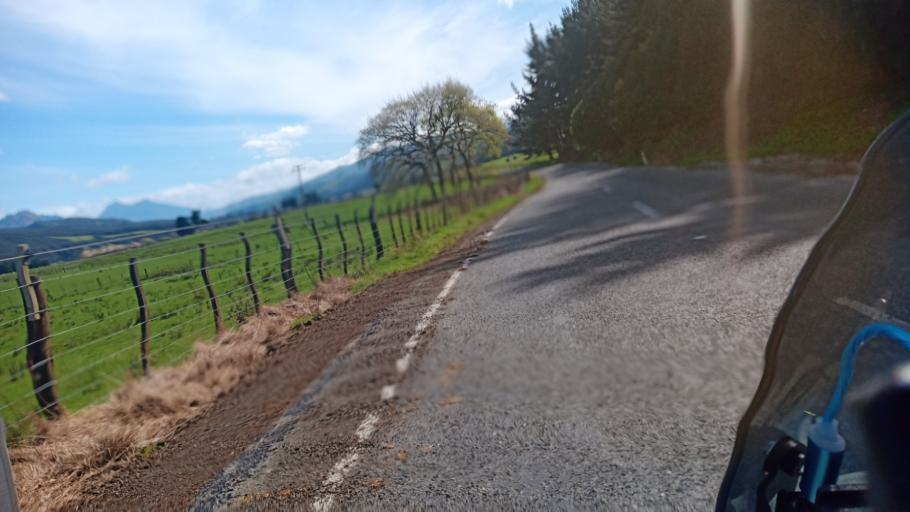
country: NZ
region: Gisborne
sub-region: Gisborne District
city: Gisborne
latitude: -37.8789
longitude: 178.2919
